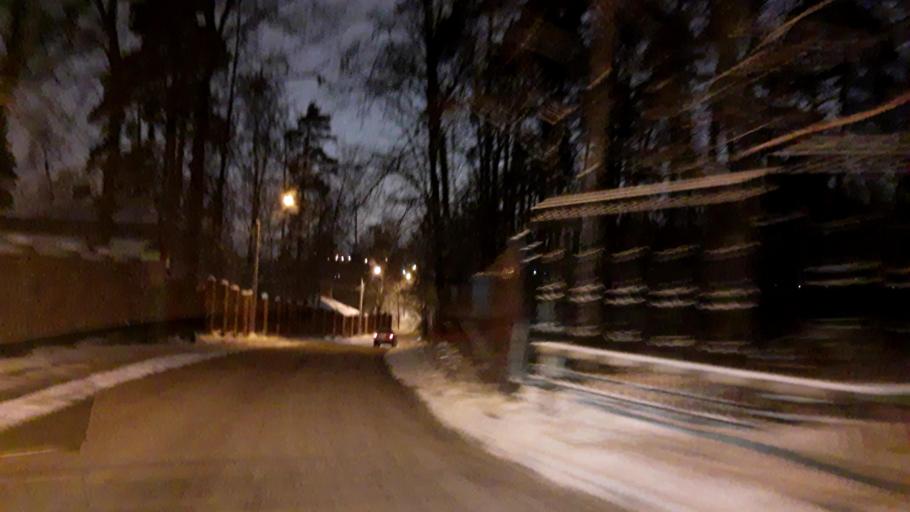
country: RU
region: Moskovskaya
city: Biryulevo Zapadnoye
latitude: 55.5694
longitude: 37.6288
